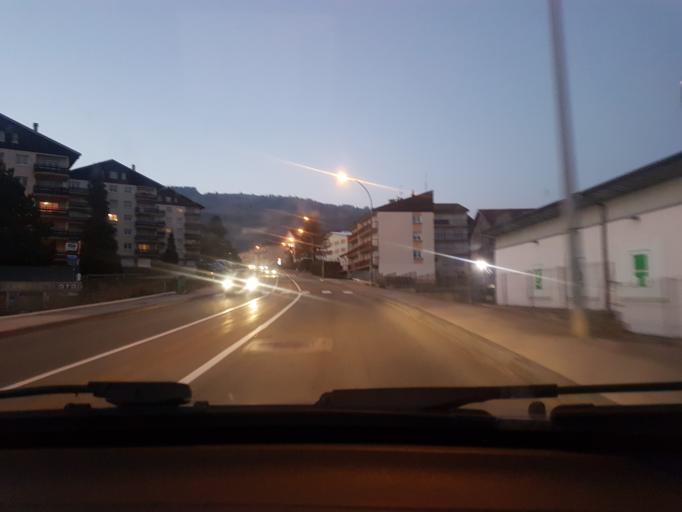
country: FR
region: Franche-Comte
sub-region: Departement du Doubs
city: Morteau
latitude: 47.0578
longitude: 6.6115
